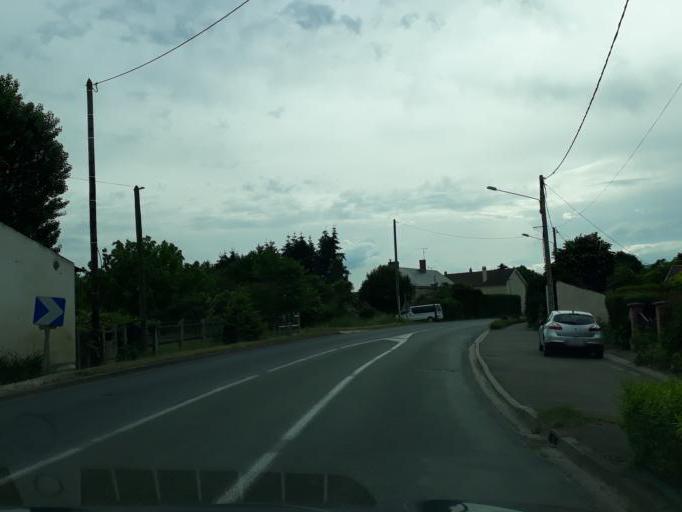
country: FR
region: Centre
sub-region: Departement du Loiret
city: Darvoy
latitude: 47.8536
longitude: 2.0934
